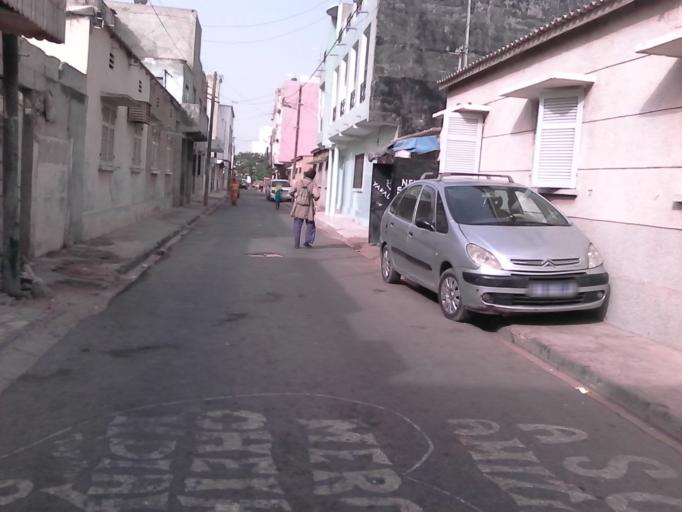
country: SN
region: Dakar
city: Grand Dakar
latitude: 14.7079
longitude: -17.4588
